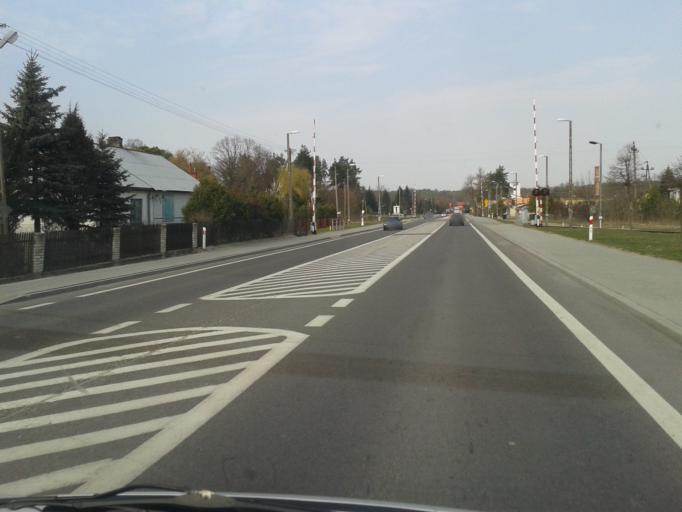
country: PL
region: Lublin Voivodeship
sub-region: Powiat tomaszowski
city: Belzec
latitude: 50.3804
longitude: 23.4433
